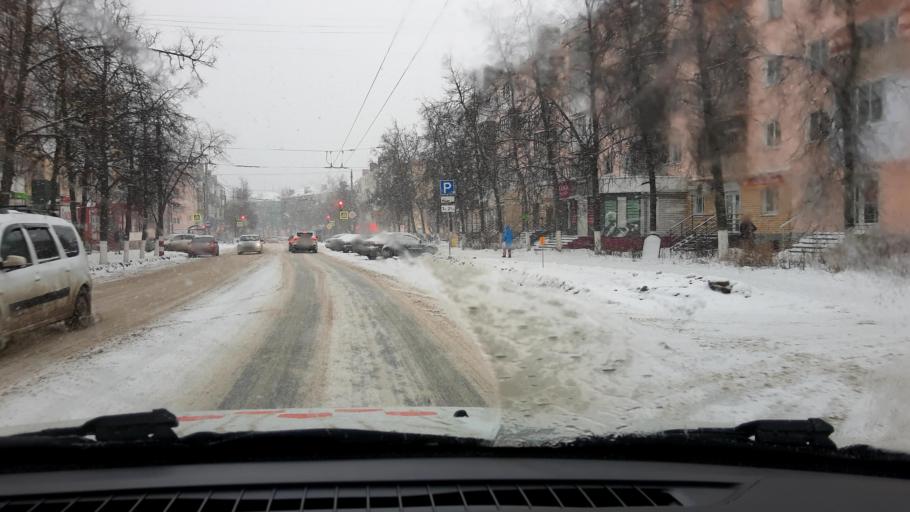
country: RU
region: Nizjnij Novgorod
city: Dzerzhinsk
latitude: 56.2386
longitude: 43.4496
